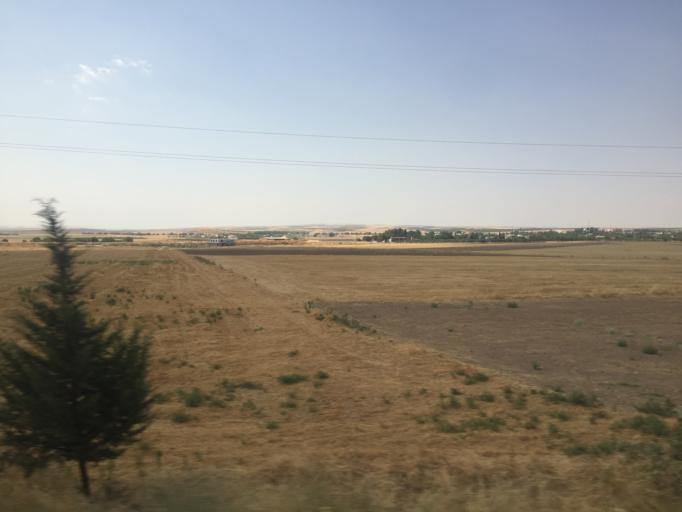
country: TR
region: Sanliurfa
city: Akziyaret
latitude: 37.3394
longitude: 38.8042
